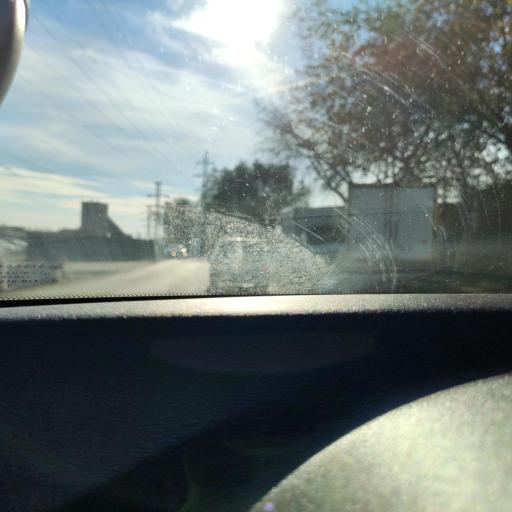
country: RU
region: Samara
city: Petra-Dubrava
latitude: 53.2527
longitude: 50.2946
